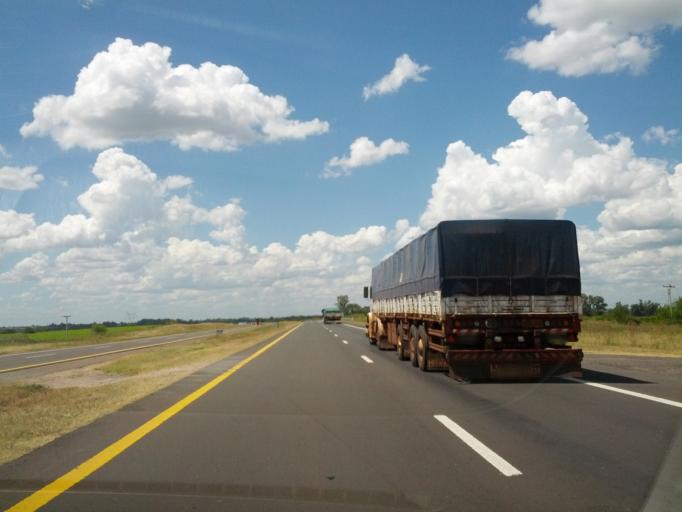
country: AR
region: Entre Rios
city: Concepcion del Uruguay
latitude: -32.5269
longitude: -58.3314
